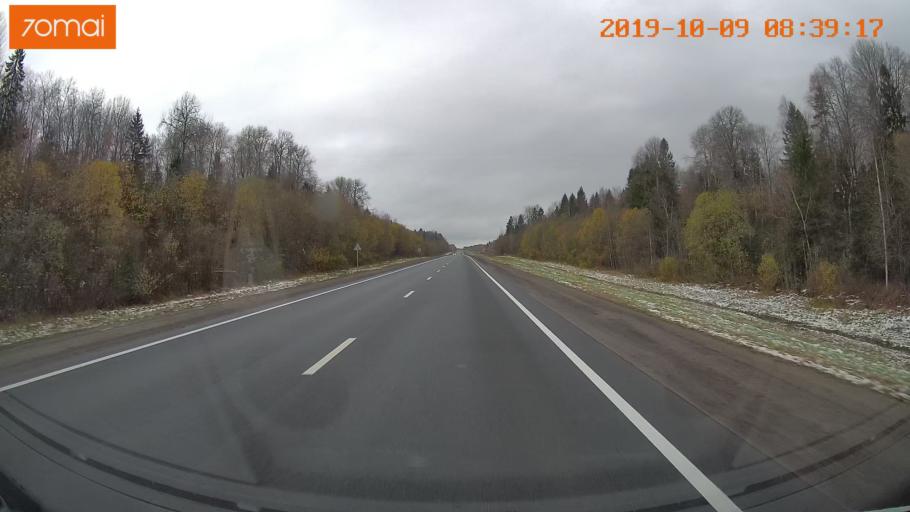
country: RU
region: Vologda
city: Gryazovets
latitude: 58.9690
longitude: 40.1548
